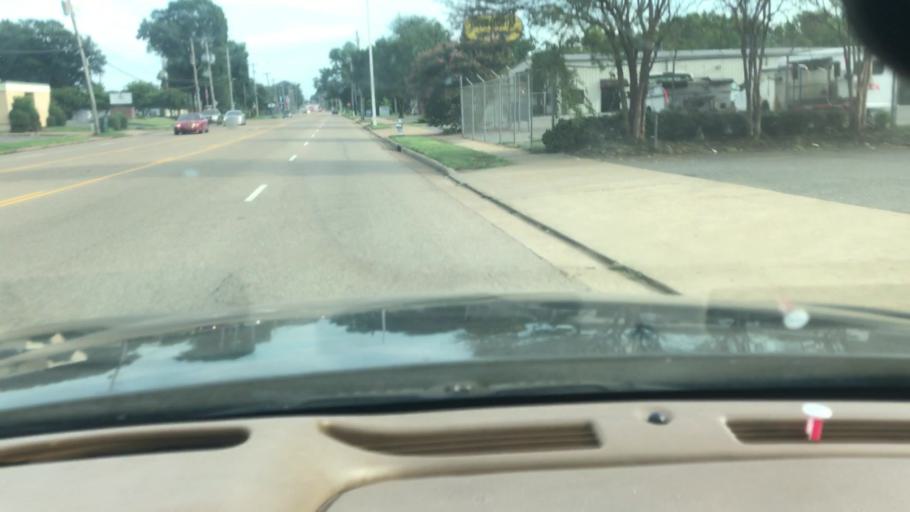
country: US
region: Tennessee
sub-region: Shelby County
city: New South Memphis
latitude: 35.0589
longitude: -90.0074
